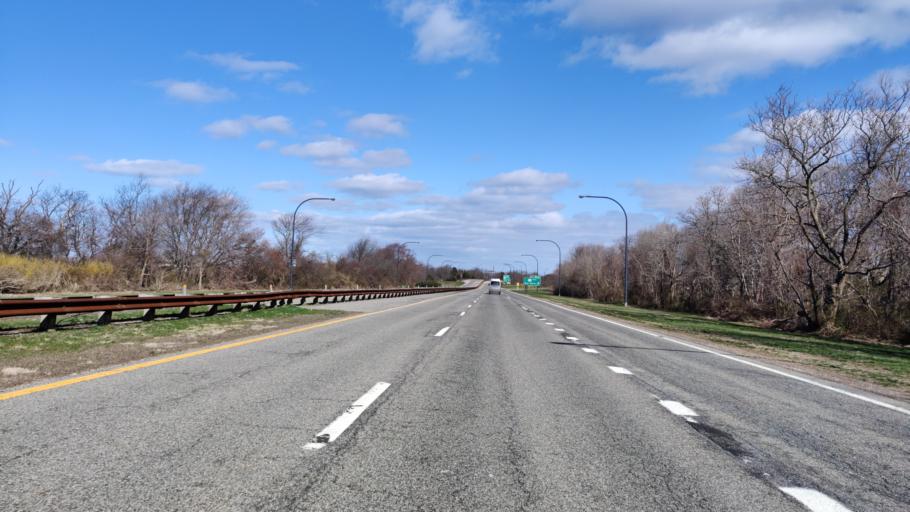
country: US
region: New York
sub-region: Suffolk County
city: West Bay Shore
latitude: 40.6919
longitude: -73.2846
